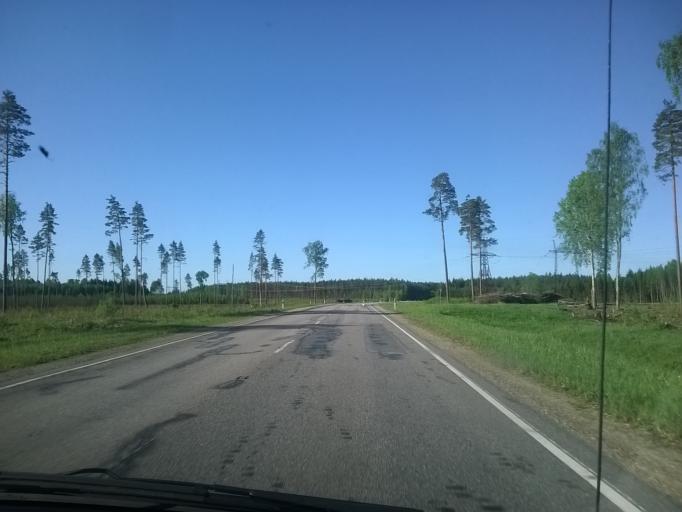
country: EE
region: Valgamaa
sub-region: Valga linn
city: Valga
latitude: 57.8821
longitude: 26.1633
